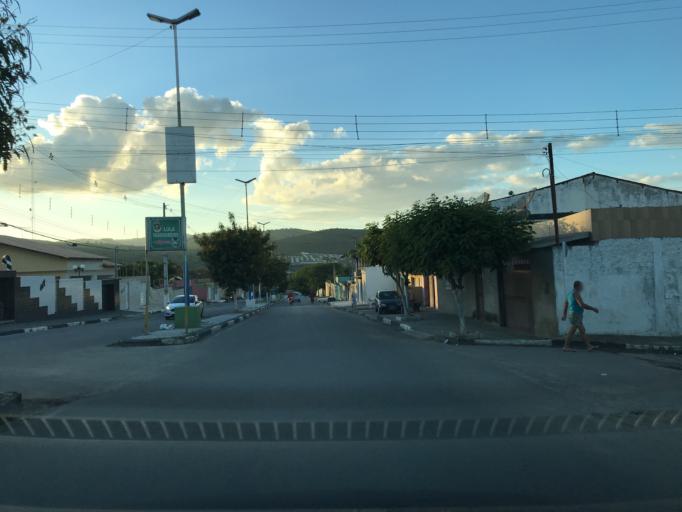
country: BR
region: Pernambuco
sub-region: Bezerros
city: Bezerros
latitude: -8.2411
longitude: -35.7600
